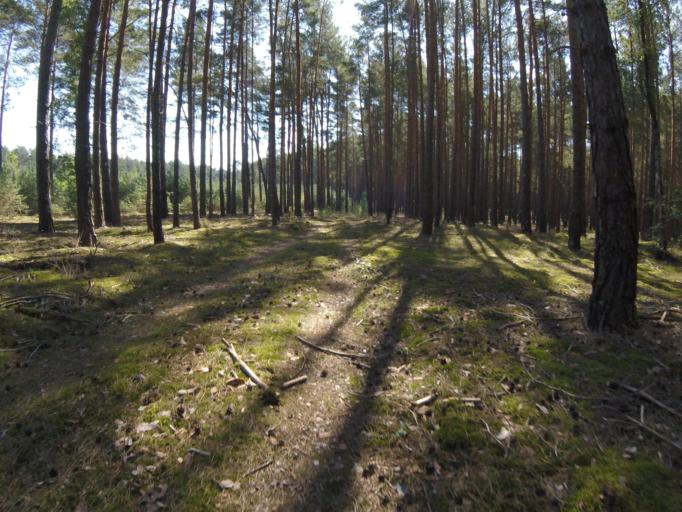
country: DE
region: Brandenburg
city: Bestensee
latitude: 52.2737
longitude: 13.6744
